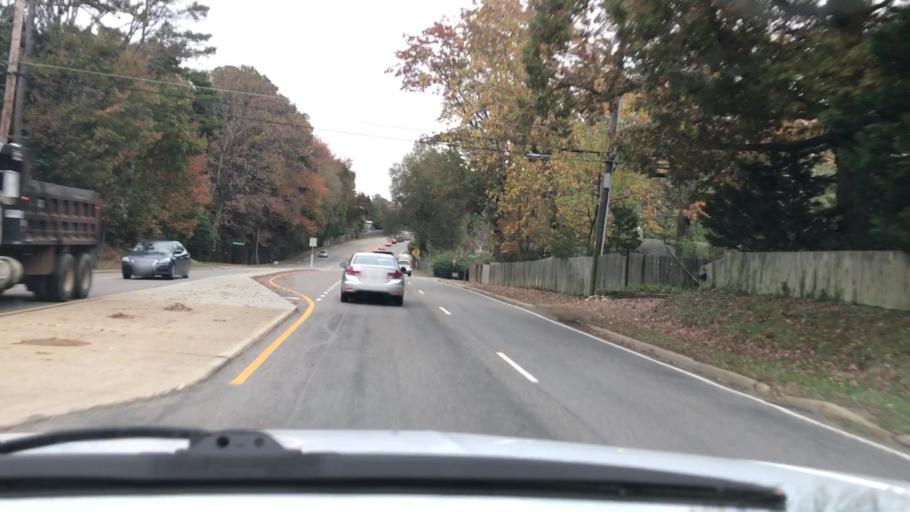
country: US
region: Virginia
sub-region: Henrico County
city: Tuckahoe
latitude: 37.5931
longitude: -77.5384
